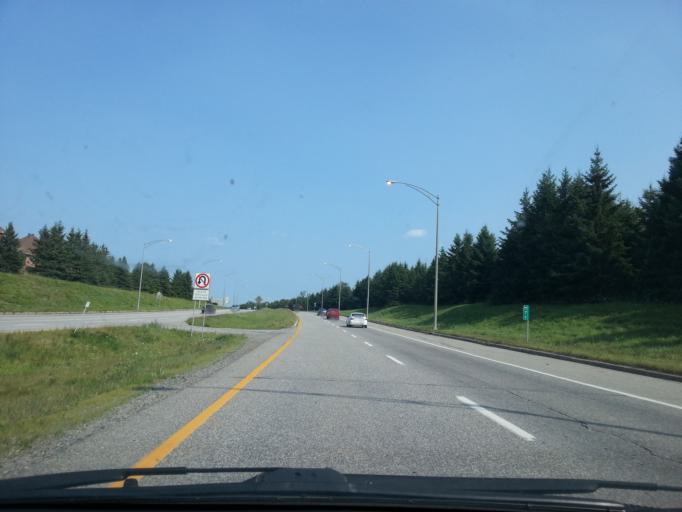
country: CA
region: Quebec
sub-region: Outaouais
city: Gatineau
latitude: 45.4721
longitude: -75.7721
